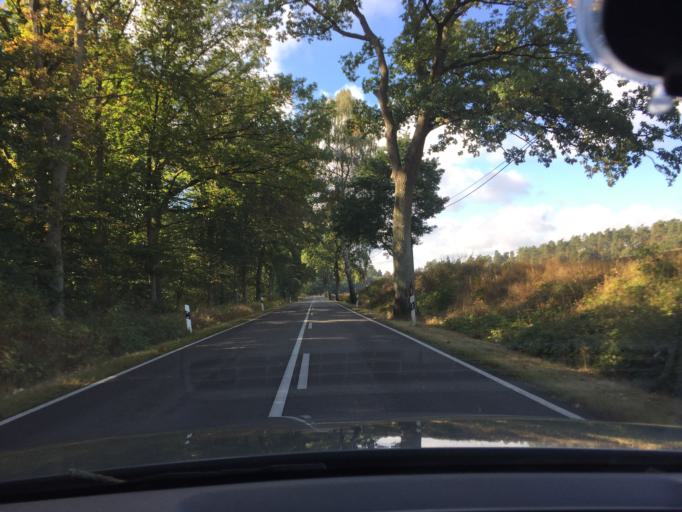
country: DE
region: Mecklenburg-Vorpommern
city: Krakow am See
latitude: 53.6733
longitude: 12.2801
